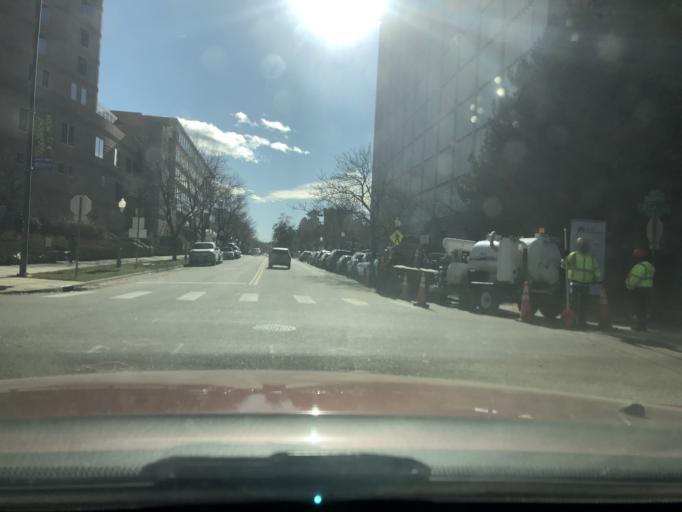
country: US
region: Colorado
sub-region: Denver County
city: Denver
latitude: 39.7483
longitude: -104.9684
